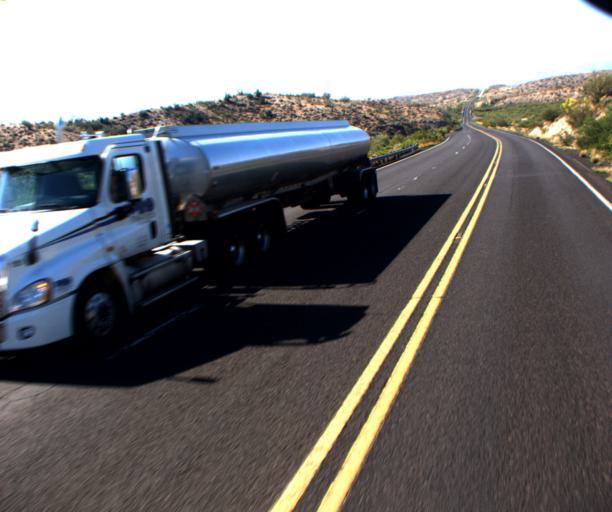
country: US
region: Arizona
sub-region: Mohave County
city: Kingman
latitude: 34.9259
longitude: -113.6586
